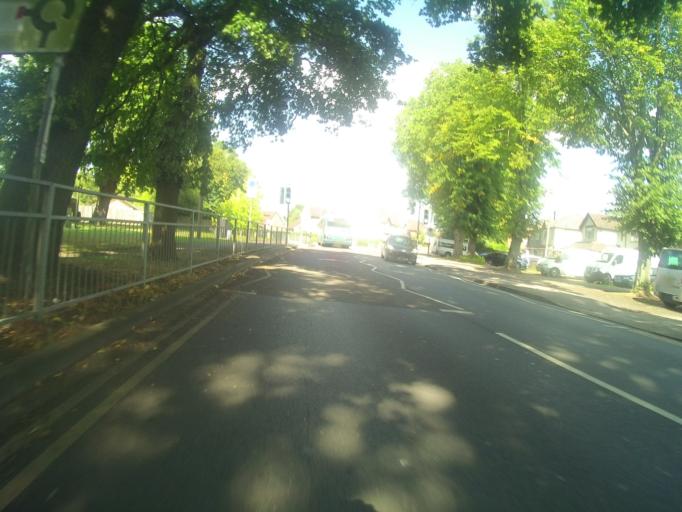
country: GB
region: England
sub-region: Surrey
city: Woking
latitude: 51.3154
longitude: -0.5738
